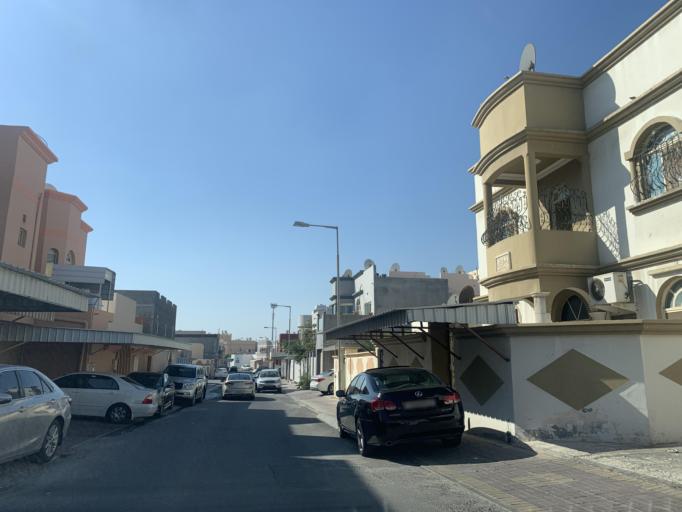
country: BH
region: Central Governorate
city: Madinat Hamad
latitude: 26.1183
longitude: 50.5068
